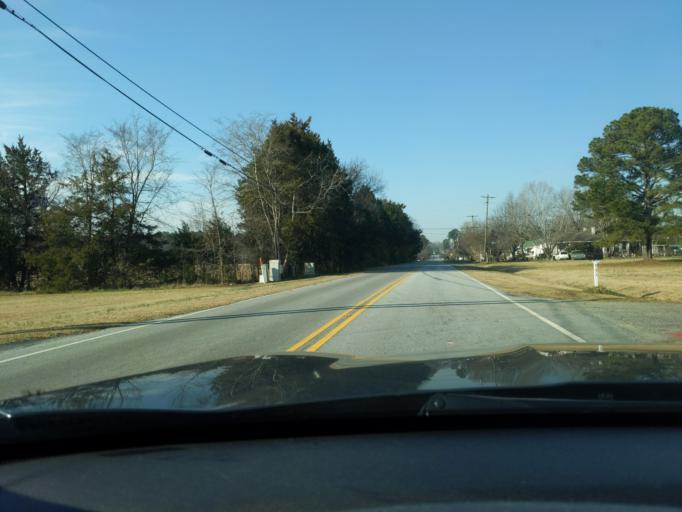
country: US
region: South Carolina
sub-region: Abbeville County
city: Calhoun Falls
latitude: 34.0928
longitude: -82.5763
